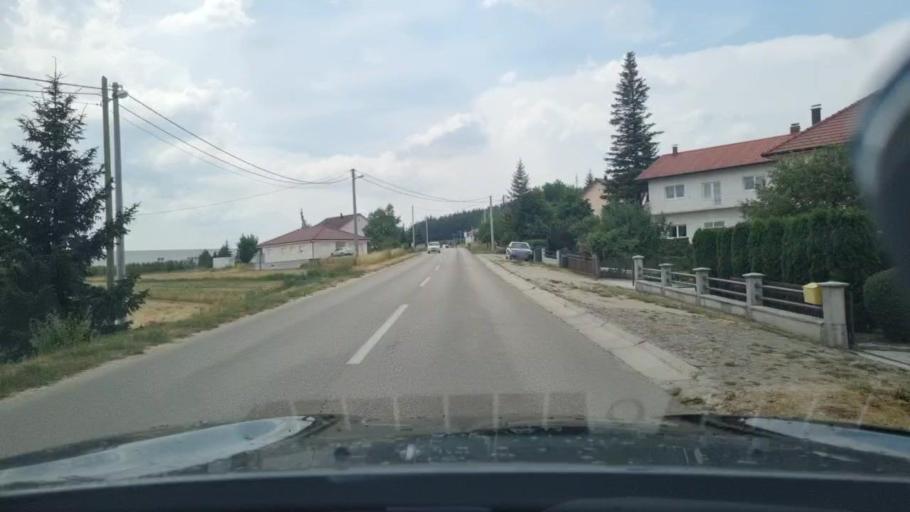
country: BA
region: Federation of Bosnia and Herzegovina
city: Tomislavgrad
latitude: 43.7037
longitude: 17.2151
